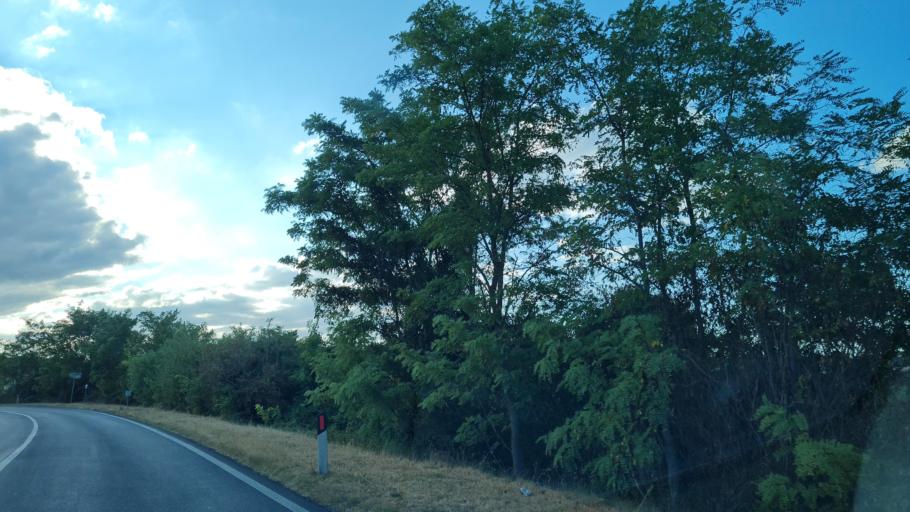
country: IT
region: Tuscany
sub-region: Provincia di Siena
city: Chianciano Terme
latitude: 43.0372
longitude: 11.8301
